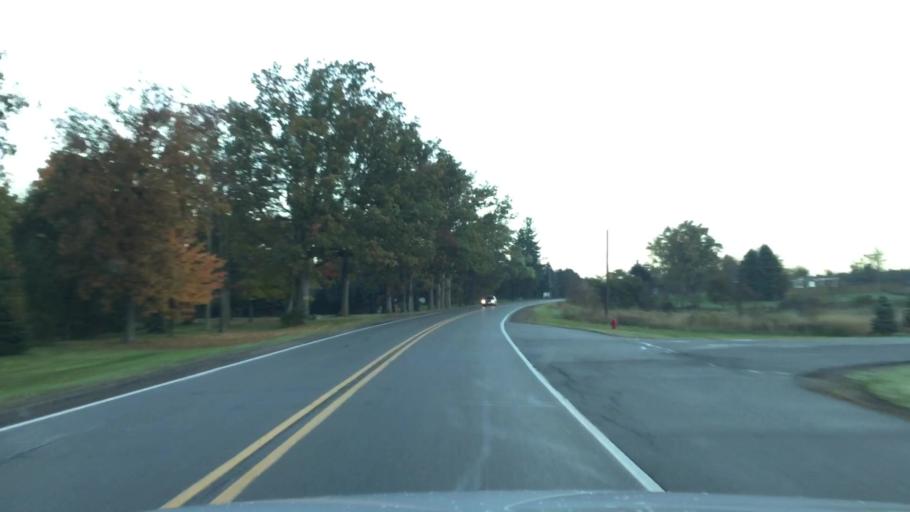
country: US
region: Michigan
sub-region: Livingston County
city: Howell
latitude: 42.6424
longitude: -83.9347
